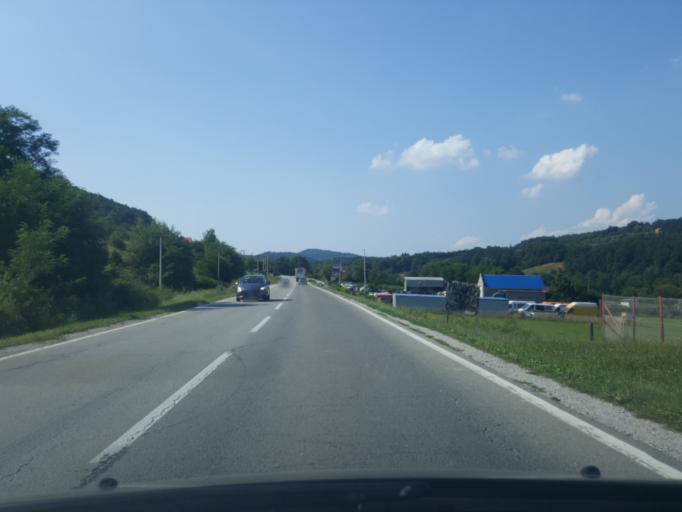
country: RS
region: Central Serbia
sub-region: Moravicki Okrug
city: Gornji Milanovac
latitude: 44.0697
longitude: 20.4906
